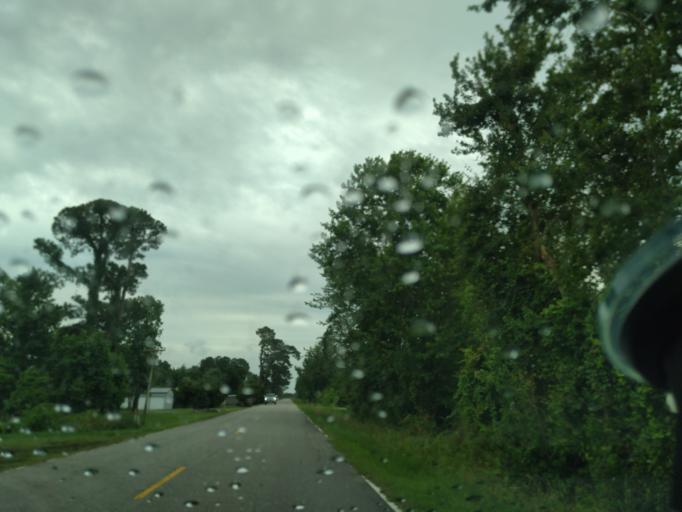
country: US
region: North Carolina
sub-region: Beaufort County
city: Belhaven
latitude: 35.7619
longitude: -76.5214
